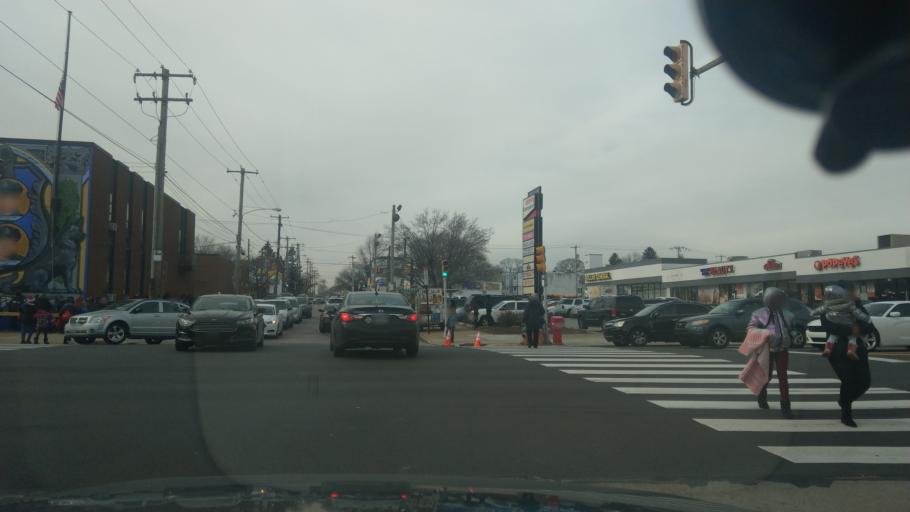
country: US
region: Pennsylvania
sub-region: Montgomery County
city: Wyncote
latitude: 40.0444
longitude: -75.1434
